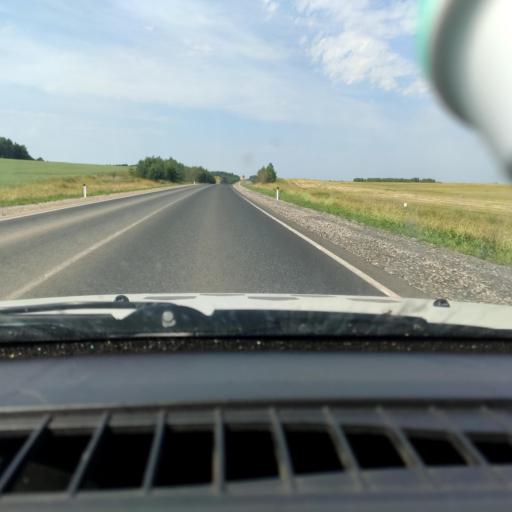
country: RU
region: Perm
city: Siva
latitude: 58.4090
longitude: 54.4729
